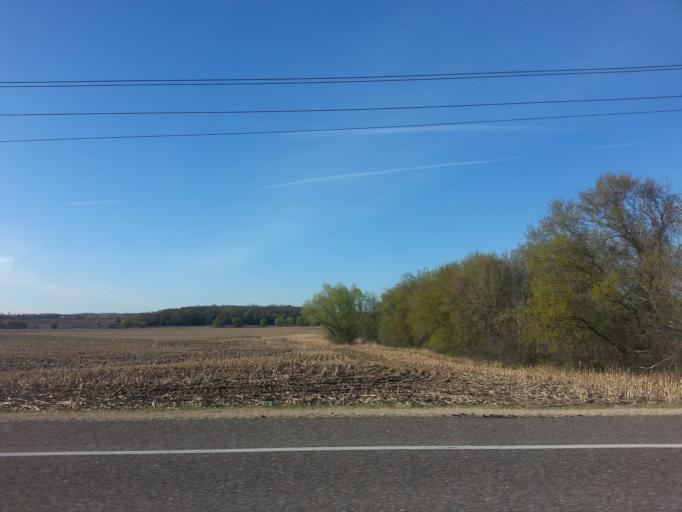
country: US
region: Minnesota
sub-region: Dakota County
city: Lakeville
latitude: 44.6235
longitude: -93.2688
